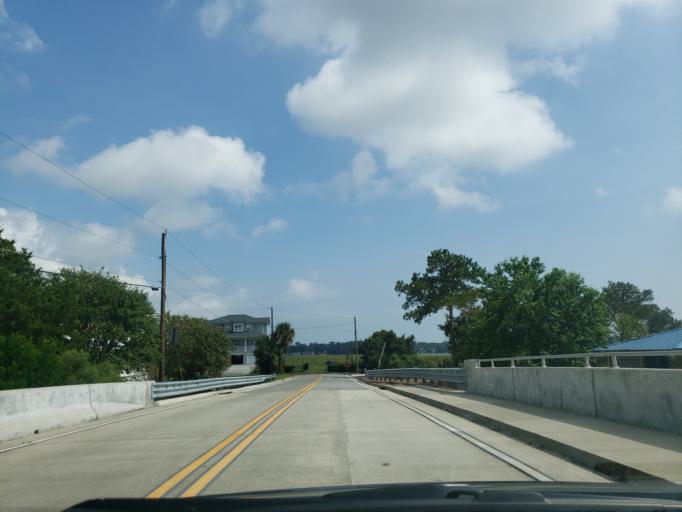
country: US
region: Georgia
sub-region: Chatham County
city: Skidaway Island
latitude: 31.9283
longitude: -81.0841
